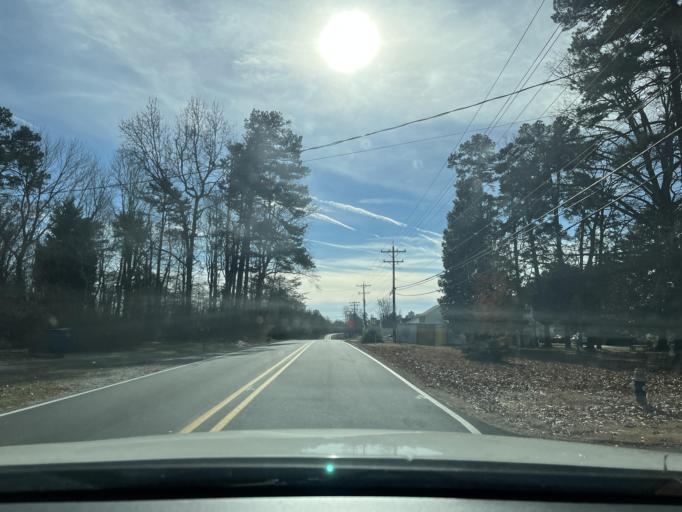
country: US
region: North Carolina
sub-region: Guilford County
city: Pleasant Garden
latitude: 36.0151
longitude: -79.7781
